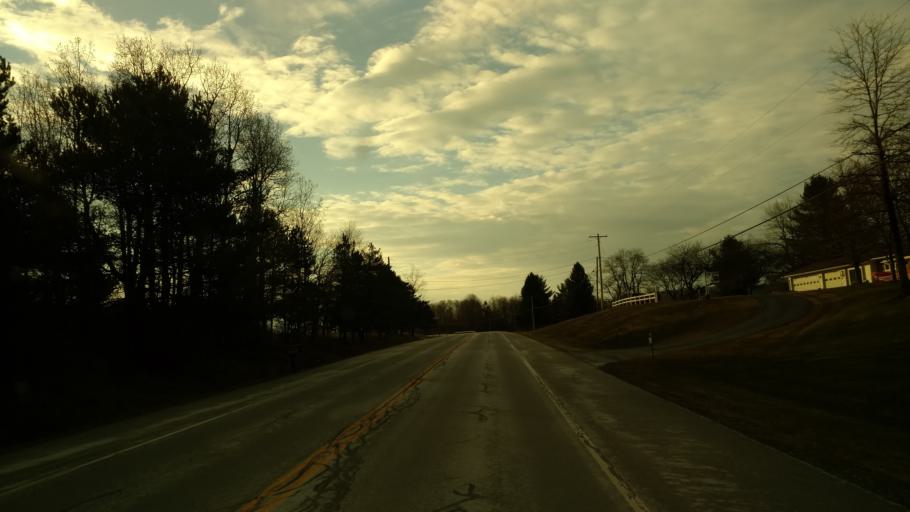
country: US
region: New York
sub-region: Allegany County
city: Wellsville
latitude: 42.0414
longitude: -77.9151
